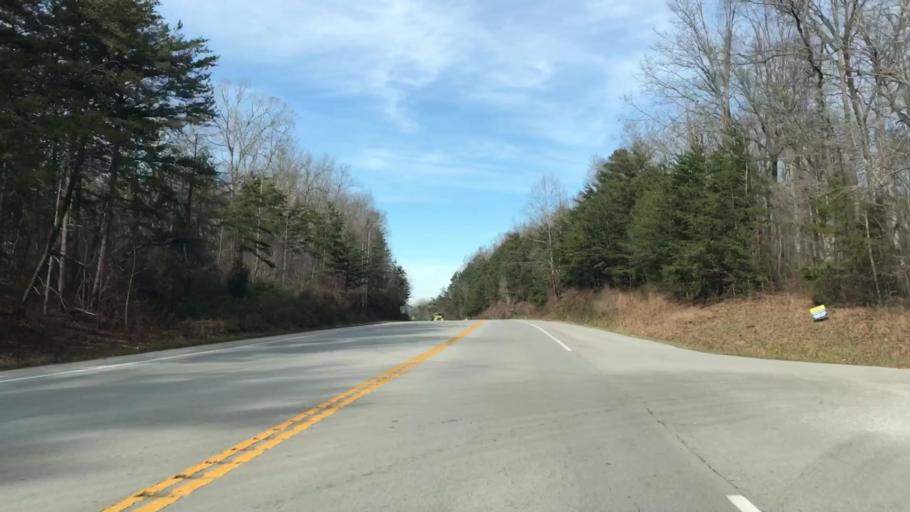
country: US
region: Kentucky
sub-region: McCreary County
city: Whitley City
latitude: 36.8962
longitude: -84.4952
